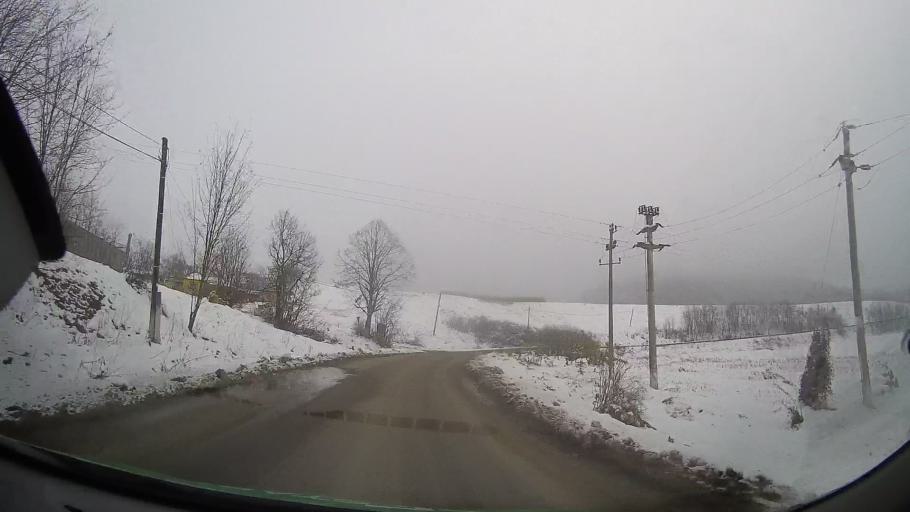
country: RO
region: Bacau
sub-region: Comuna Vultureni
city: Vultureni
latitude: 46.3979
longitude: 27.2757
